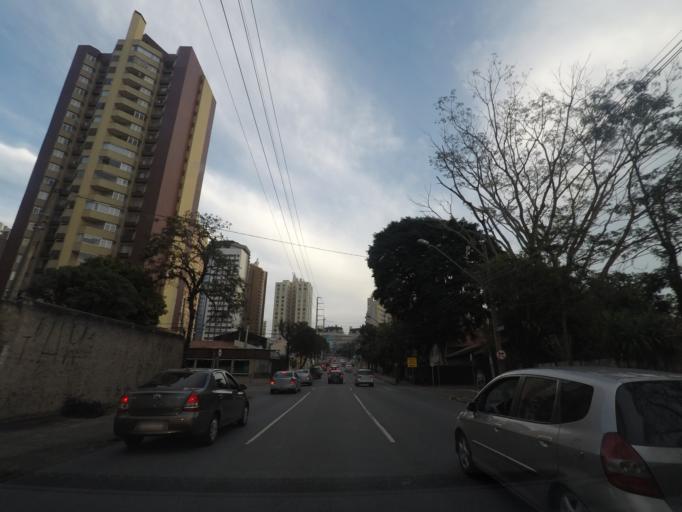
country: BR
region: Parana
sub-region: Curitiba
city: Curitiba
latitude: -25.4058
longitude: -49.2547
